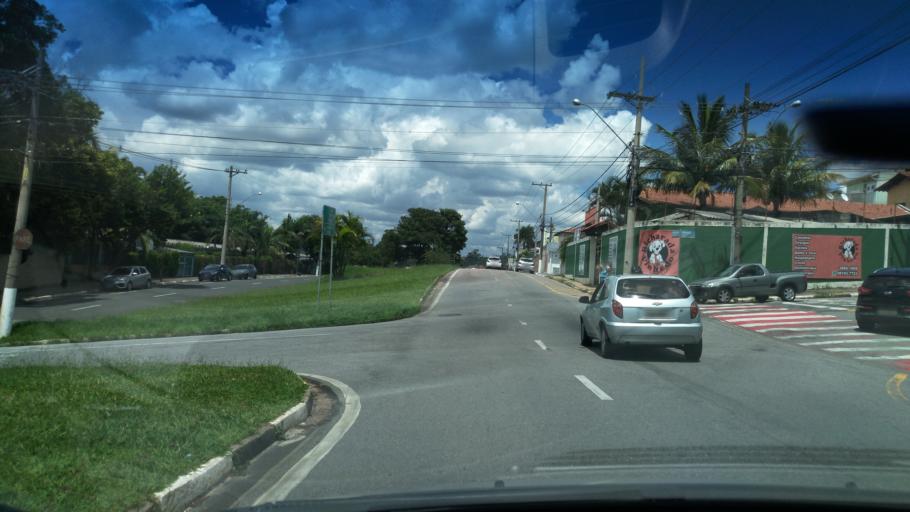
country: BR
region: Sao Paulo
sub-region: Vinhedo
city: Vinhedo
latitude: -23.0287
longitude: -46.9812
